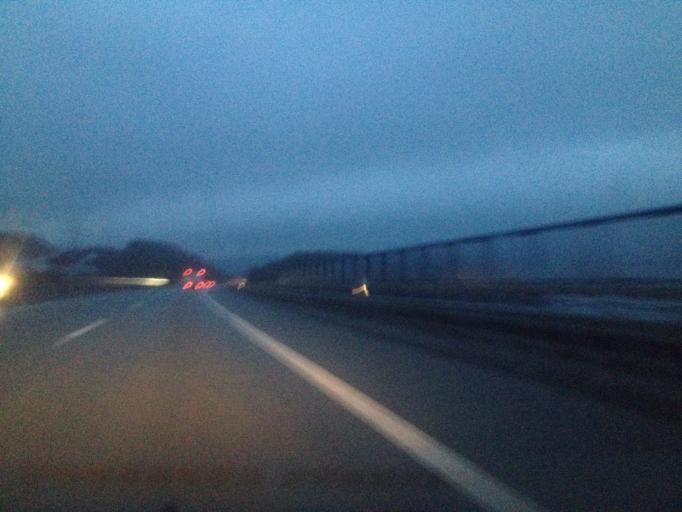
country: DE
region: Rheinland-Pfalz
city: Bad Neuenahr-Ahrweiler
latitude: 50.5659
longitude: 7.1442
